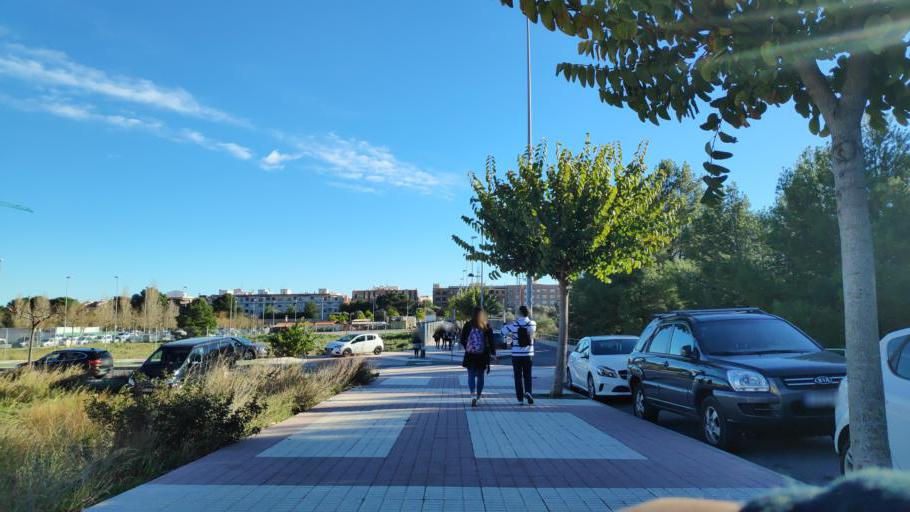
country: ES
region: Valencia
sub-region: Provincia de Castello
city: Benicassim
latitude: 40.0577
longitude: 0.0592
